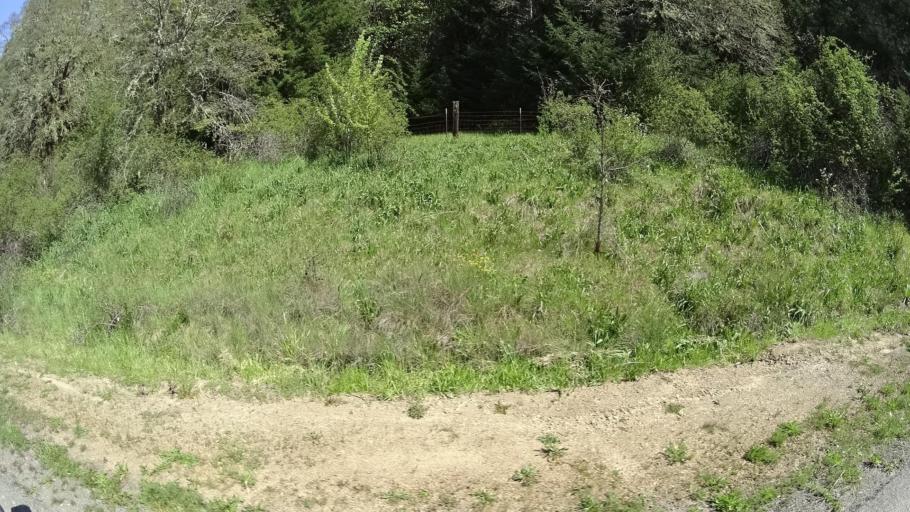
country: US
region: California
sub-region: Humboldt County
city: Redway
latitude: 40.2931
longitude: -123.6504
